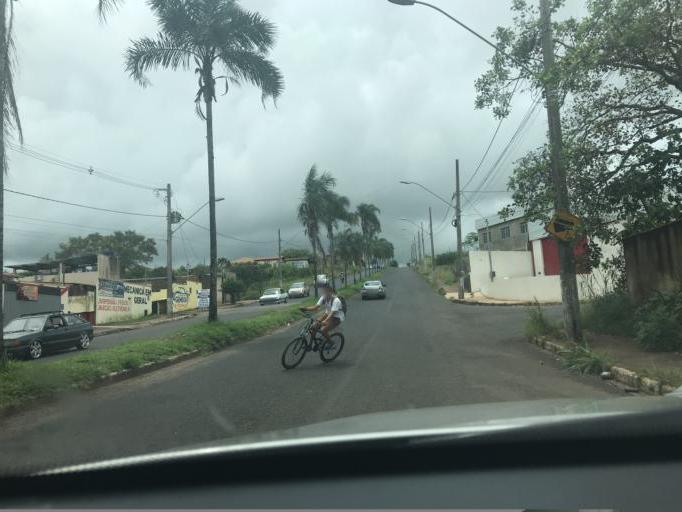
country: BR
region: Minas Gerais
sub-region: Araxa
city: Araxa
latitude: -19.5775
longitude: -46.9319
